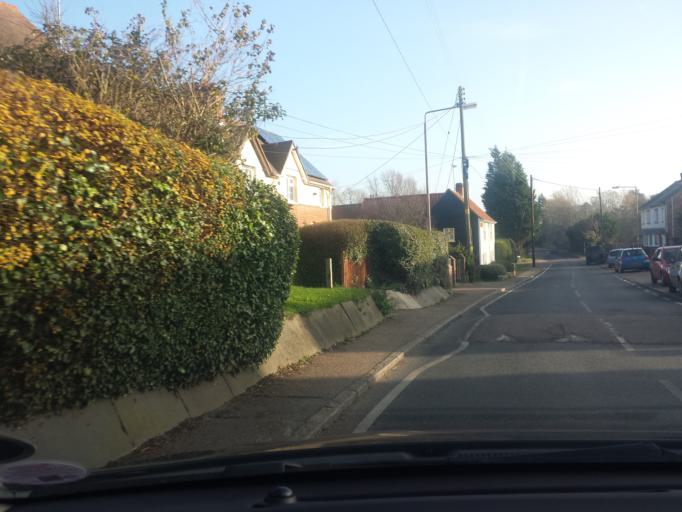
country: GB
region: England
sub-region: Essex
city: Saint Osyth
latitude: 51.7971
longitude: 1.0805
